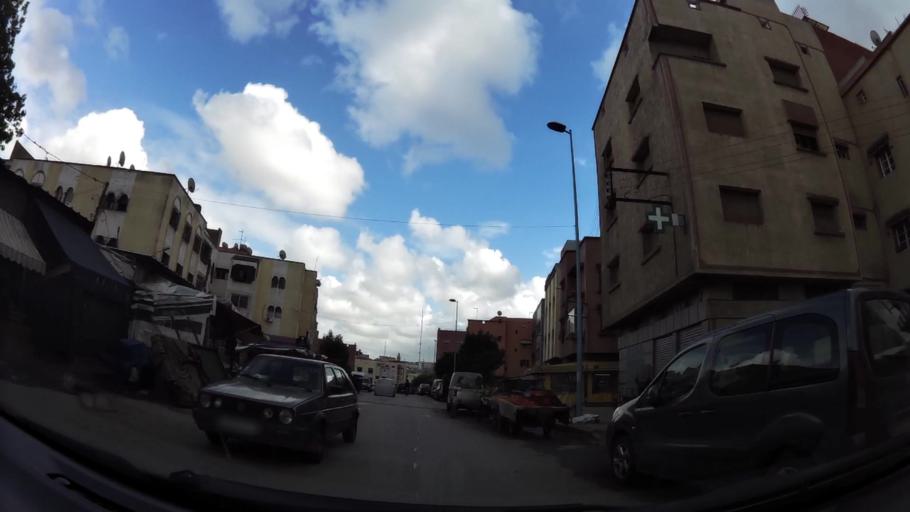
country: MA
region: Grand Casablanca
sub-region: Casablanca
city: Casablanca
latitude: 33.5456
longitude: -7.5868
